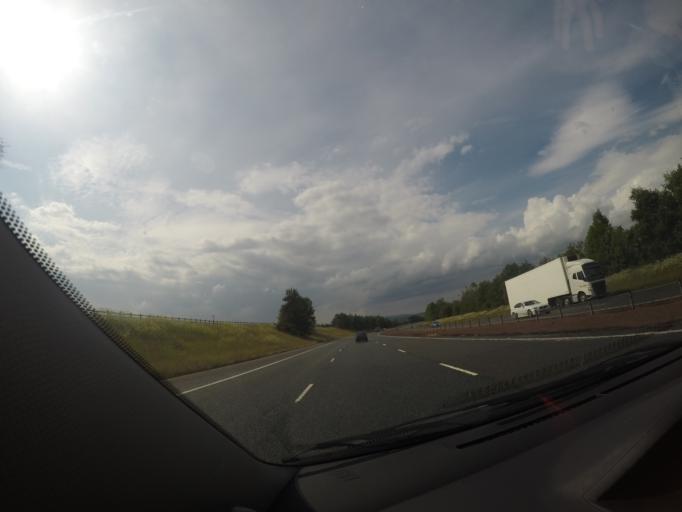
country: GB
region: Scotland
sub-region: Dumfries and Galloway
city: Lochmaben
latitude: 55.1752
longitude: -3.4002
